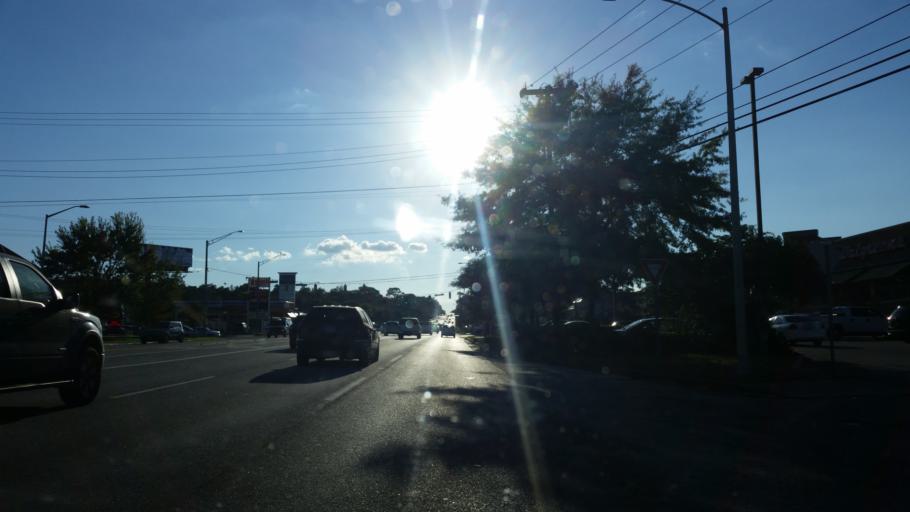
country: US
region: Alabama
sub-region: Mobile County
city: Tillmans Corner
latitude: 30.6762
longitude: -88.1473
